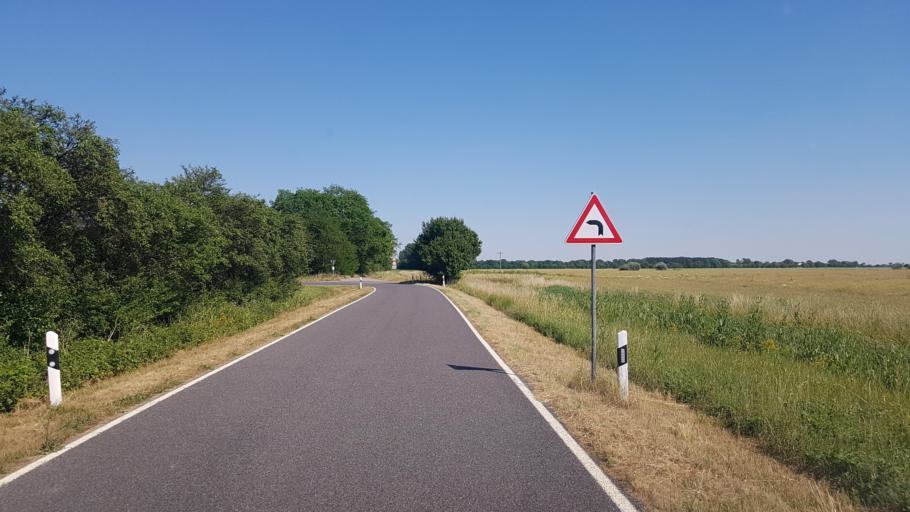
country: DE
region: Saxony-Anhalt
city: Elster
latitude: 51.7687
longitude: 12.8598
